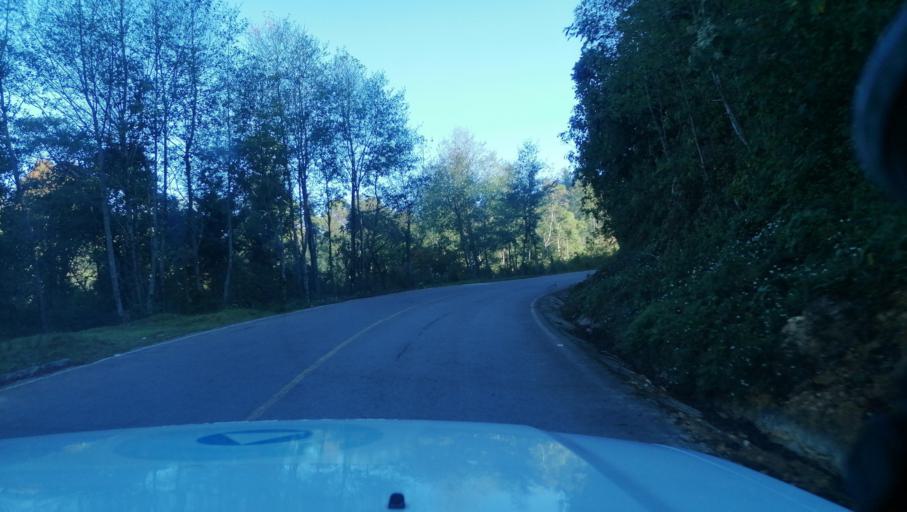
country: MX
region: Chiapas
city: Motozintla de Mendoza
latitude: 15.2550
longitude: -92.2163
